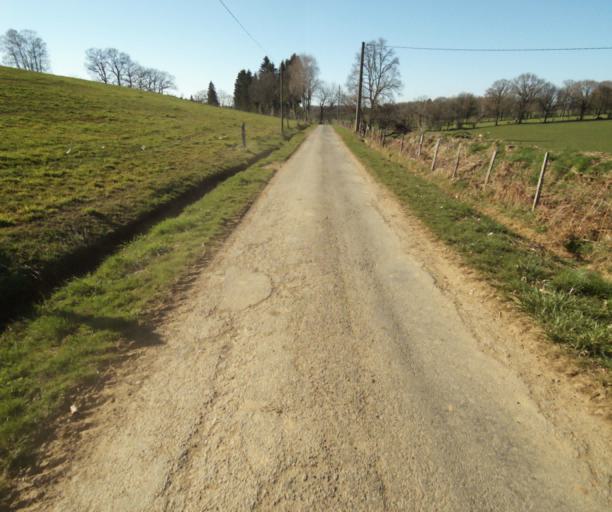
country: FR
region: Limousin
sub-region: Departement de la Correze
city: Seilhac
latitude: 45.3900
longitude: 1.6855
